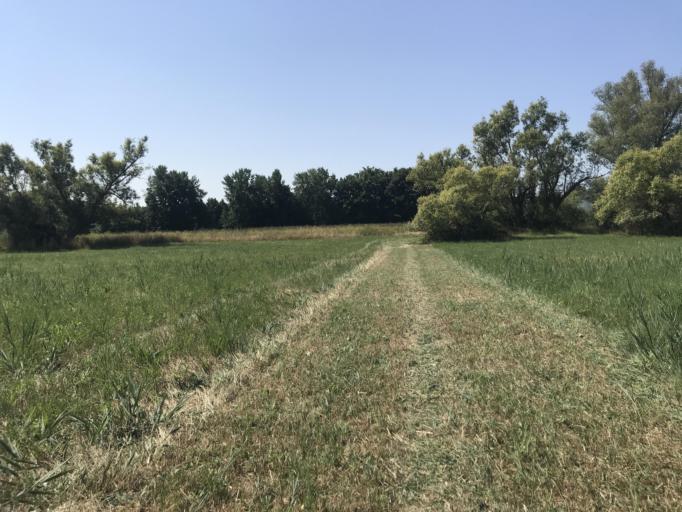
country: DE
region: Rheinland-Pfalz
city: Nieder-Olm
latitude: 49.9169
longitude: 8.1869
